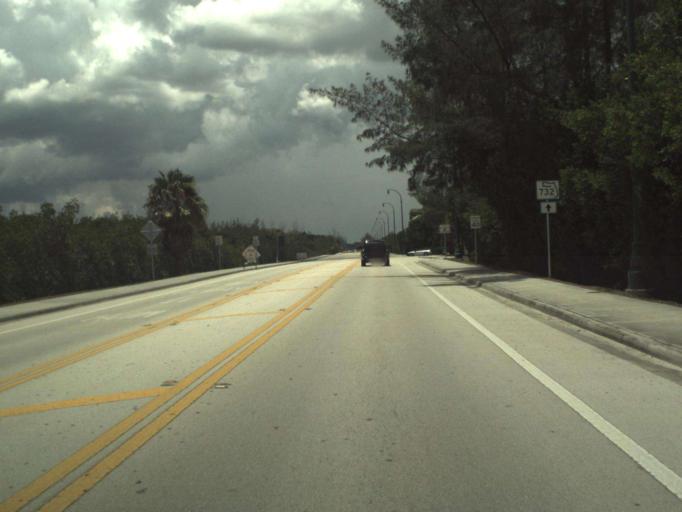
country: US
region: Florida
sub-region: Martin County
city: Jensen Beach
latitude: 27.2557
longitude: -80.1990
